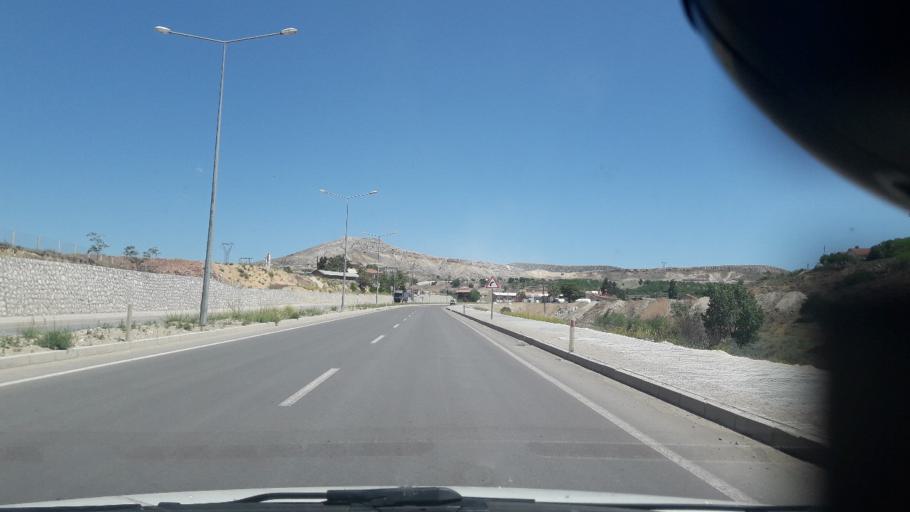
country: TR
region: Malatya
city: Hekimhan
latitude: 38.8186
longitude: 37.9394
